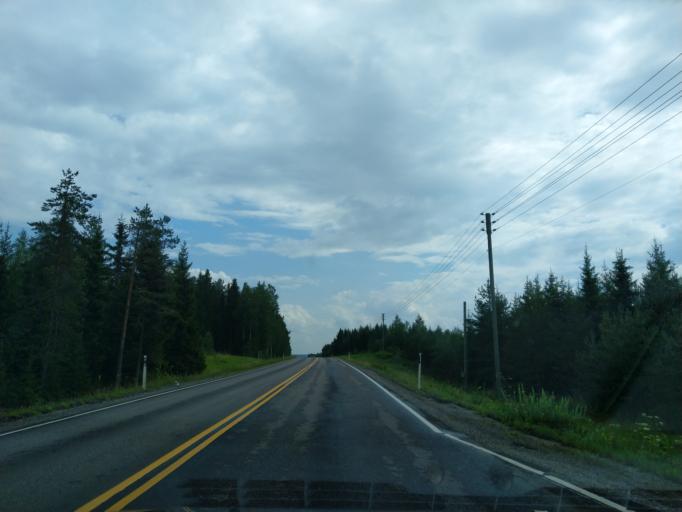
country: FI
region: South Karelia
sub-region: Imatra
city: Parikkala
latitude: 61.6171
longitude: 29.4458
